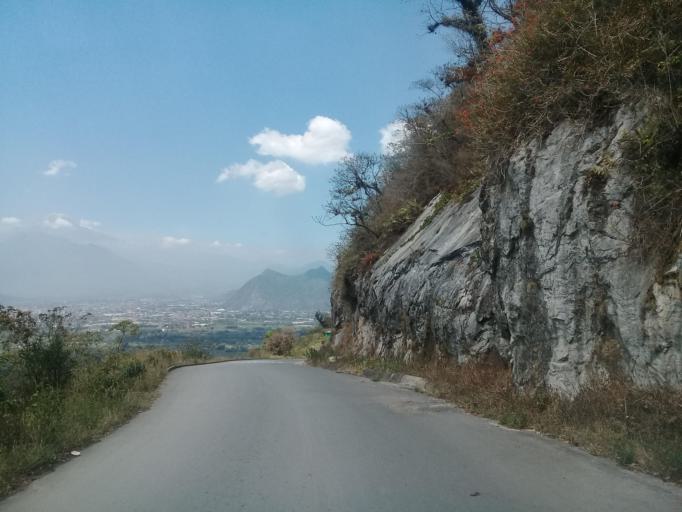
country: MX
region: Veracruz
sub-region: Tlilapan
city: Tonalixco
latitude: 18.8063
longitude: -97.0600
